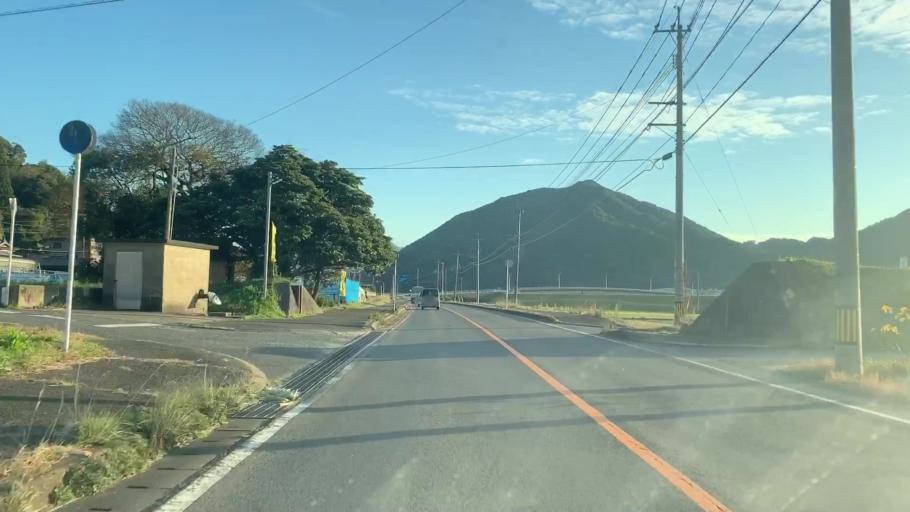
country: JP
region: Saga Prefecture
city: Karatsu
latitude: 33.3777
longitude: 129.9995
